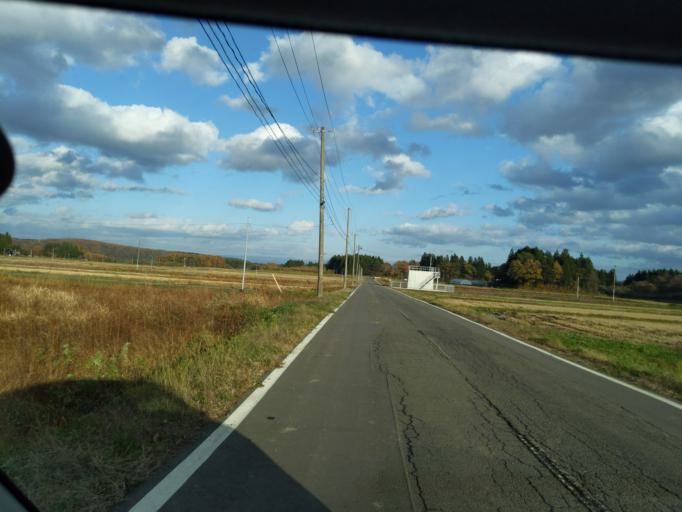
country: JP
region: Iwate
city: Mizusawa
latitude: 39.1186
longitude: 140.9783
